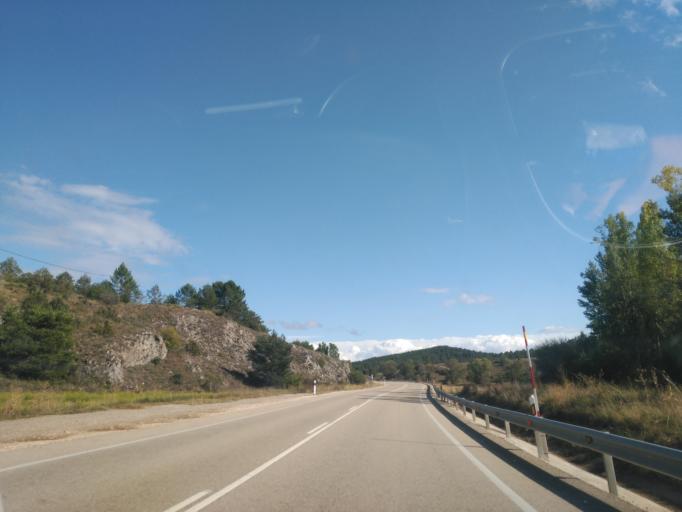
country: ES
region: Castille and Leon
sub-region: Provincia de Burgos
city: Rabanera del Pinar
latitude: 41.8708
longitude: -3.2161
